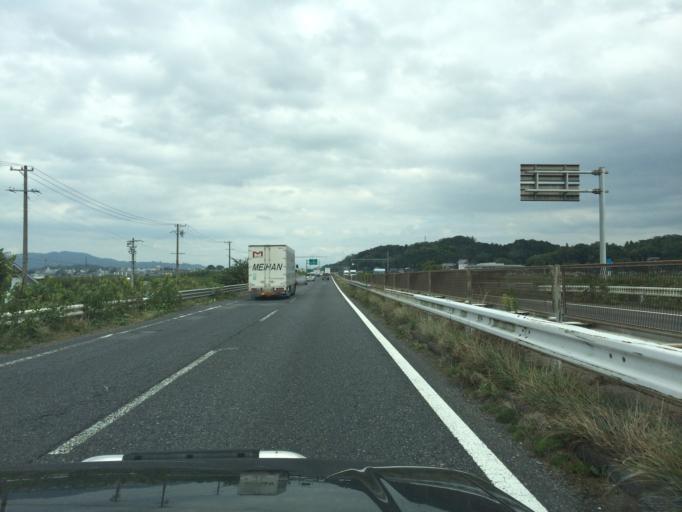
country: JP
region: Mie
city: Ueno-ebisumachi
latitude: 34.7425
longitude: 136.1161
